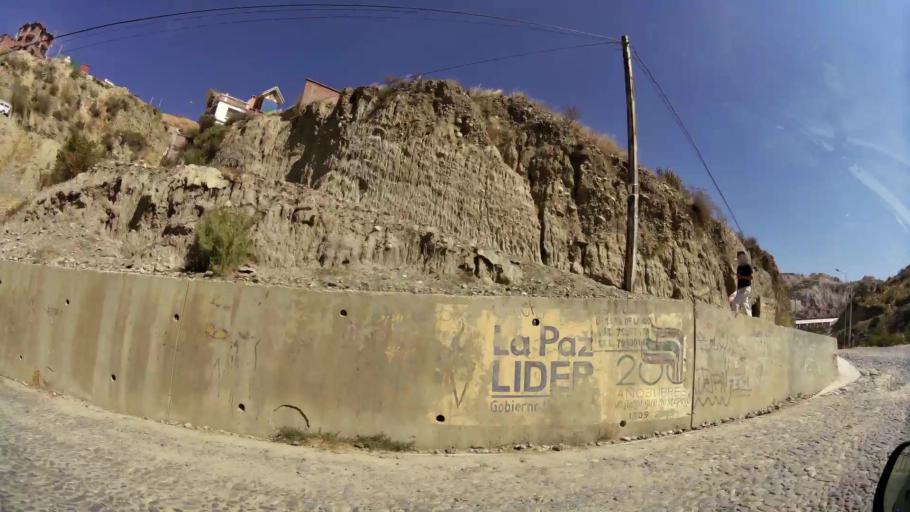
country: BO
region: La Paz
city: La Paz
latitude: -16.5390
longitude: -68.1016
